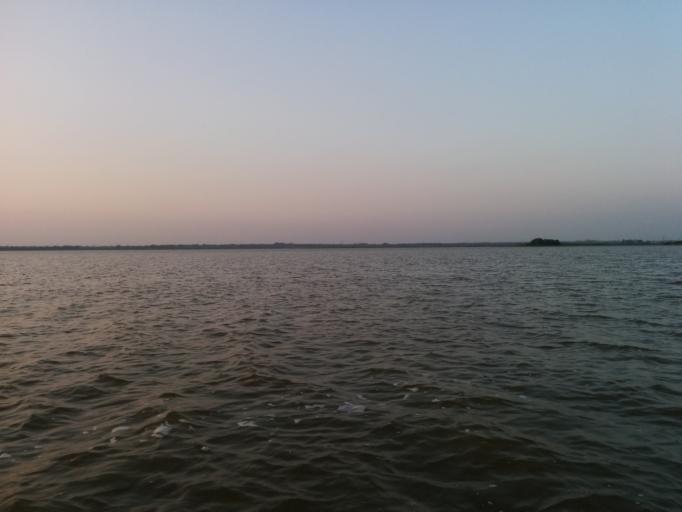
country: IN
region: Tamil Nadu
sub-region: Villupuram
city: Auroville
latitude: 11.9498
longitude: 79.7481
